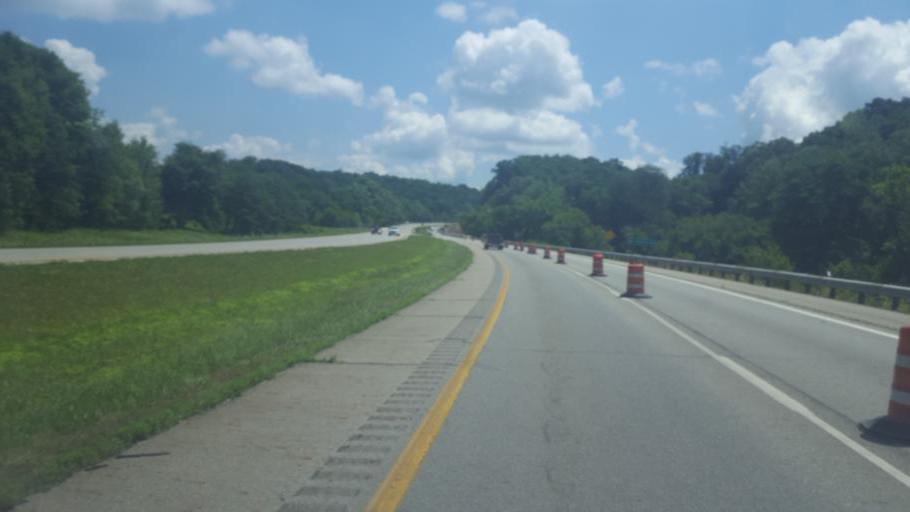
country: US
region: Ohio
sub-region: Jackson County
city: Jackson
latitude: 39.1220
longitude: -82.6978
